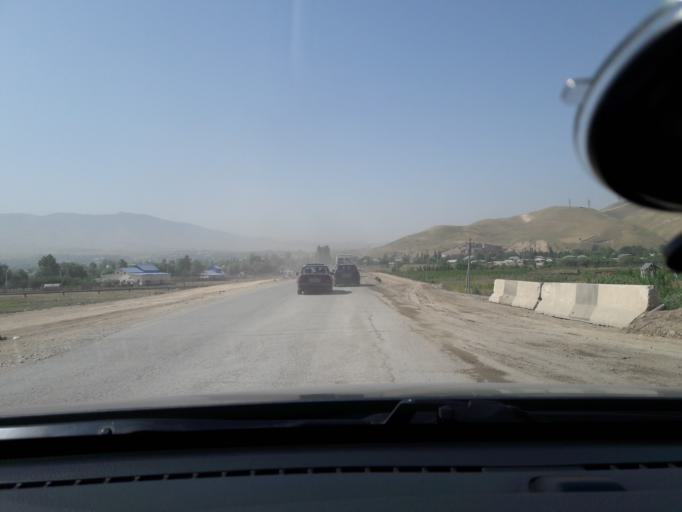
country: TJ
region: Dushanbe
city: Boshkengash
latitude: 38.4526
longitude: 68.7350
